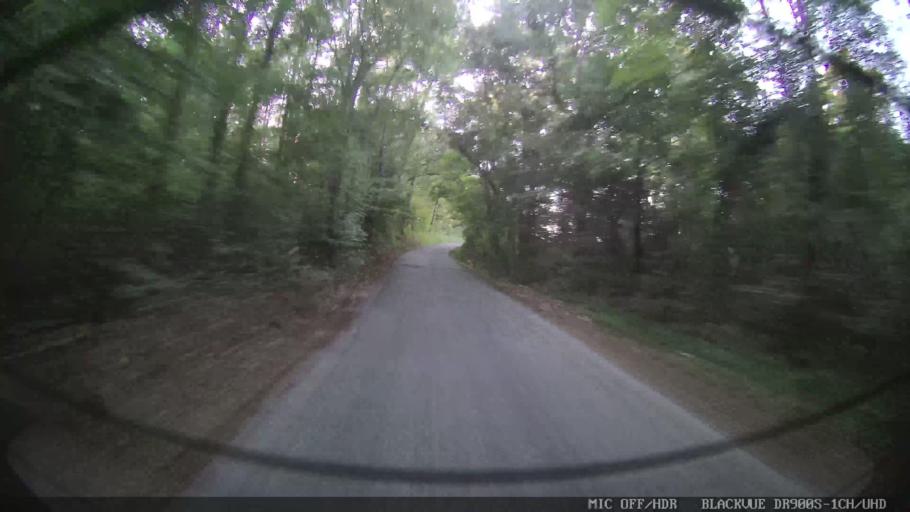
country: US
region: Tennessee
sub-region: Bradley County
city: Wildwood Lake
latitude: 35.0144
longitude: -84.7483
